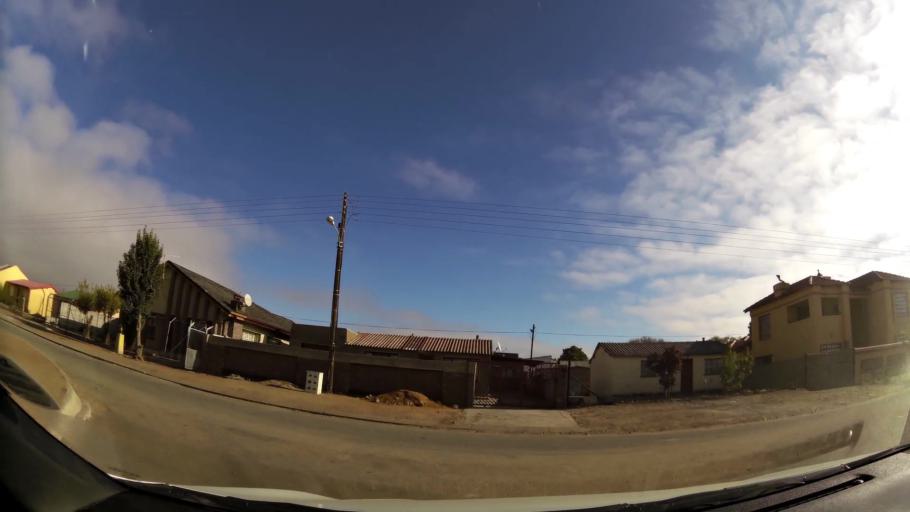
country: ZA
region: Limpopo
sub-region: Capricorn District Municipality
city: Polokwane
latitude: -23.8438
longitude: 29.3916
